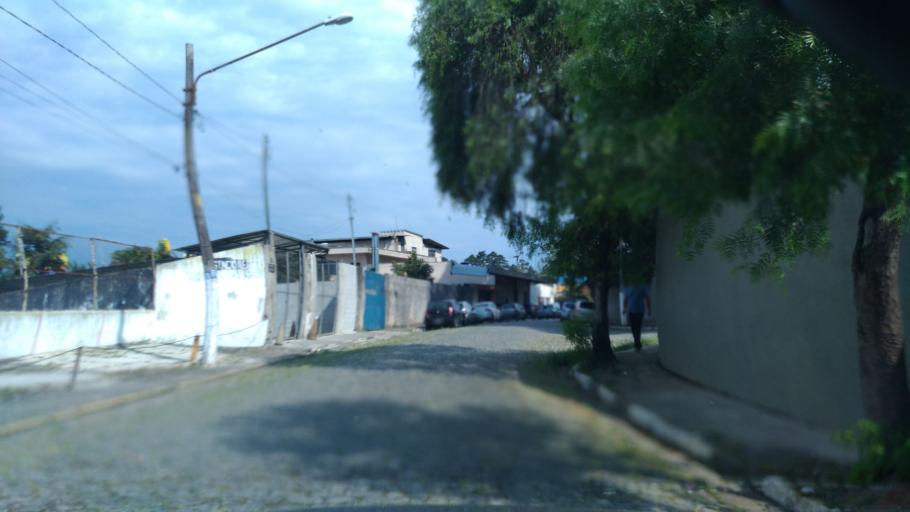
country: BR
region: Sao Paulo
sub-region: Sao Bernardo Do Campo
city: Sao Bernardo do Campo
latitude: -23.7770
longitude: -46.5305
